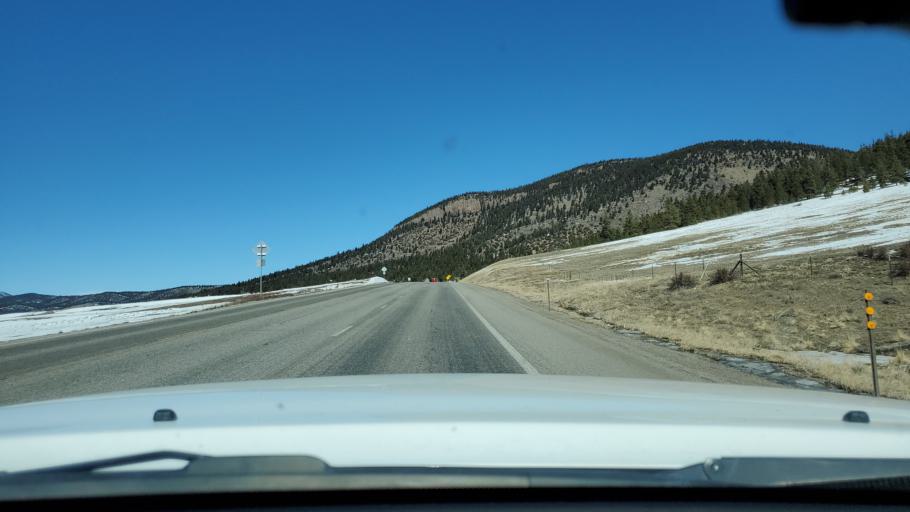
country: US
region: Colorado
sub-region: Chaffee County
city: Buena Vista
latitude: 38.8675
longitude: -105.9848
